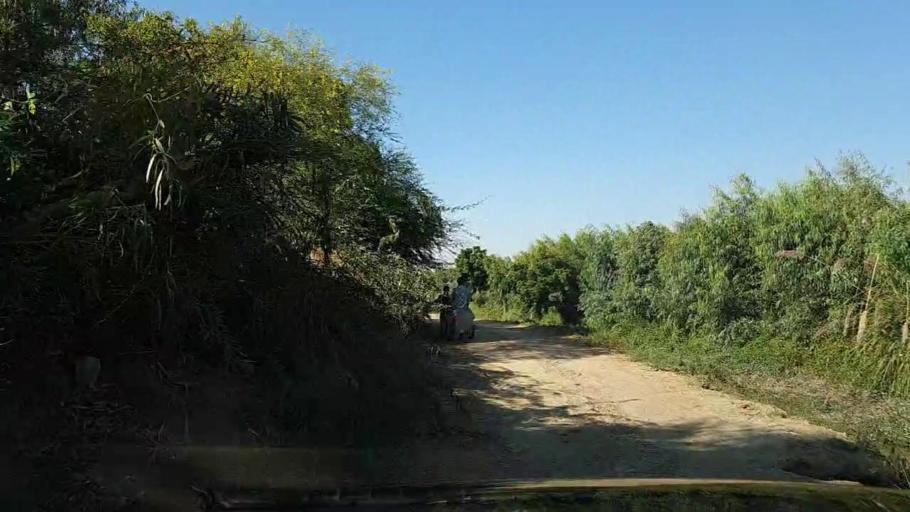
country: PK
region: Sindh
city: Thatta
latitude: 24.7074
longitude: 67.9111
